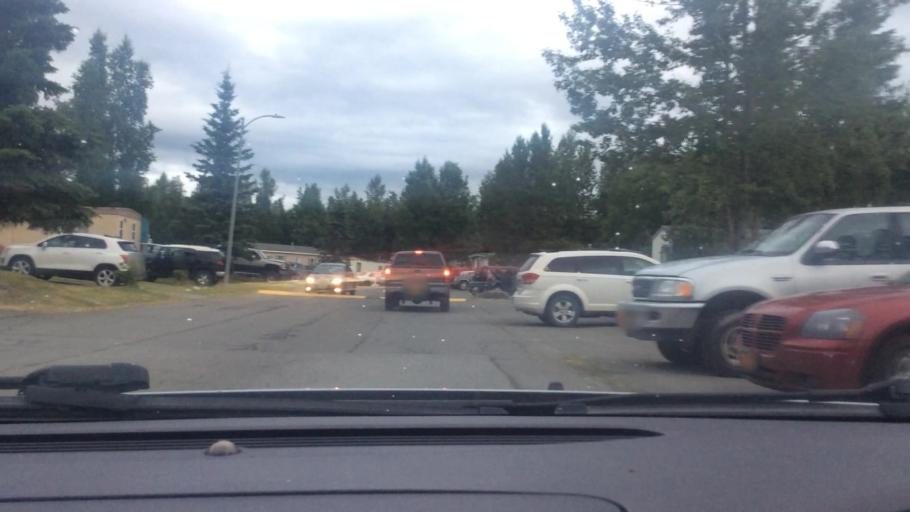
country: US
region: Alaska
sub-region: Anchorage Municipality
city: Elmendorf Air Force Base
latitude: 61.1992
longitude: -149.7273
